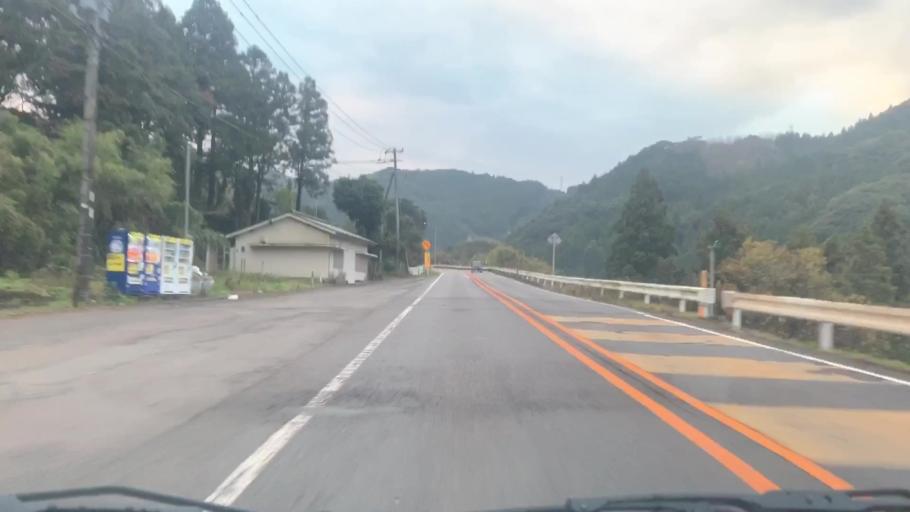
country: JP
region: Saga Prefecture
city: Ureshinomachi-shimojuku
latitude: 33.0720
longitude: 129.9611
